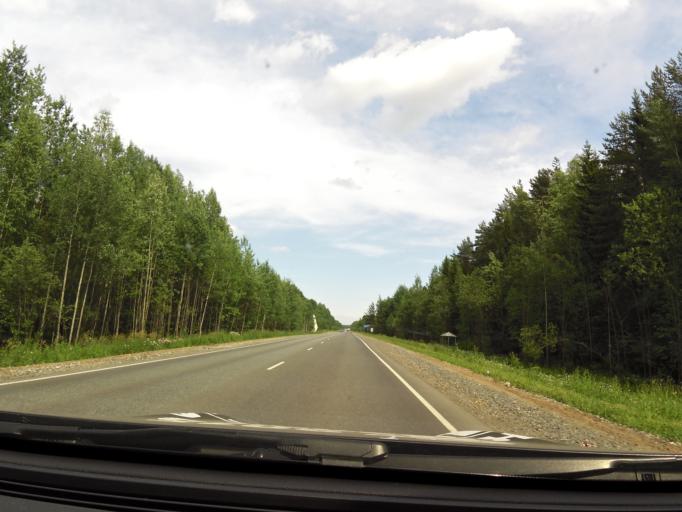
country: RU
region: Kirov
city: Slobodskoy
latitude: 58.7255
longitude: 50.2081
